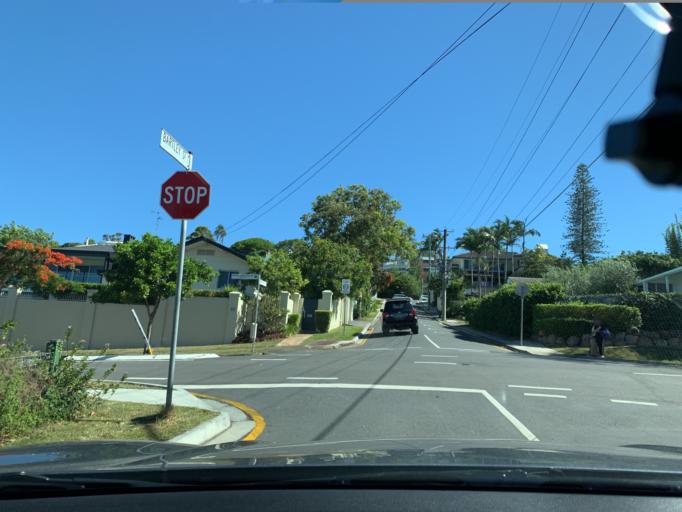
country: AU
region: Queensland
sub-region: Brisbane
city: Ascot
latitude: -27.4293
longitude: 153.0522
